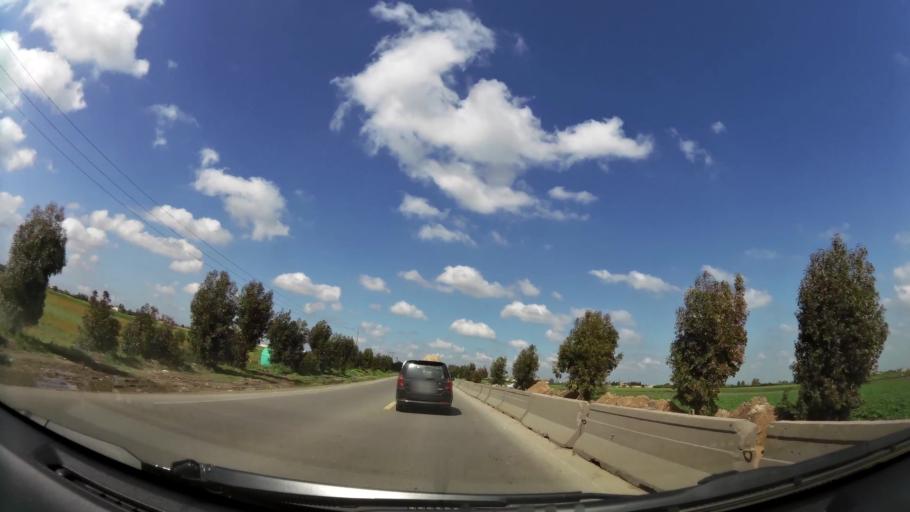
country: MA
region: Grand Casablanca
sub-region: Mediouna
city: Mediouna
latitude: 33.4187
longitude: -7.5282
